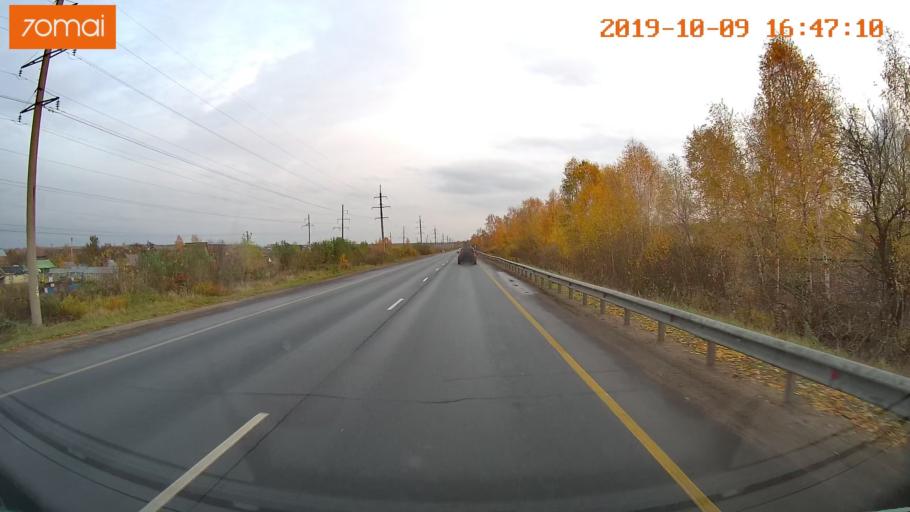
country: RU
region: Kostroma
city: Volgorechensk
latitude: 57.4389
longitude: 41.1740
